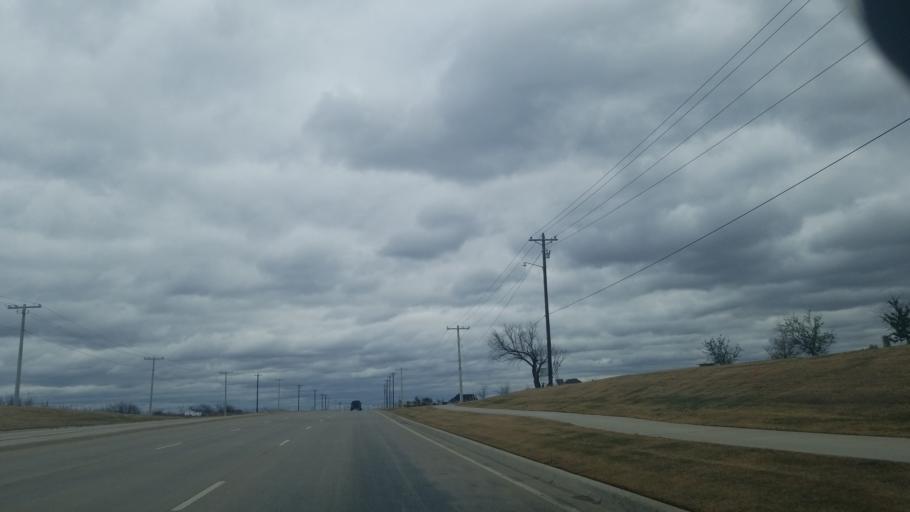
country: US
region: Texas
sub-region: Denton County
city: Roanoke
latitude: 33.0599
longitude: -97.2151
